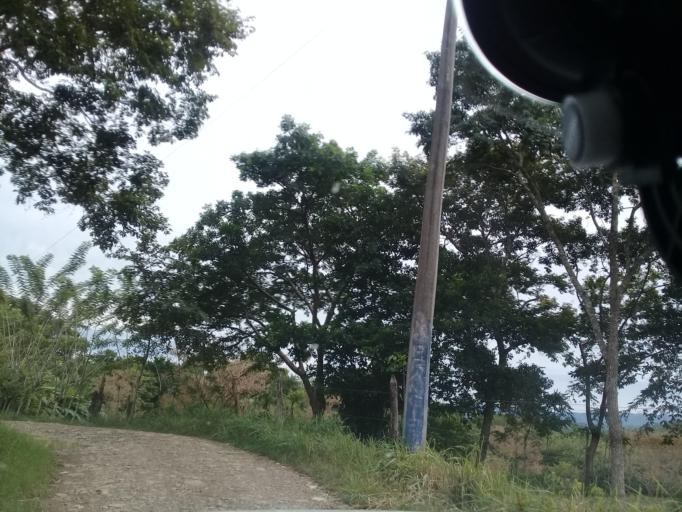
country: MX
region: Hidalgo
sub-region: Huejutla de Reyes
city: Parque de Poblamiento Solidaridad
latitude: 21.1775
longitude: -98.3781
